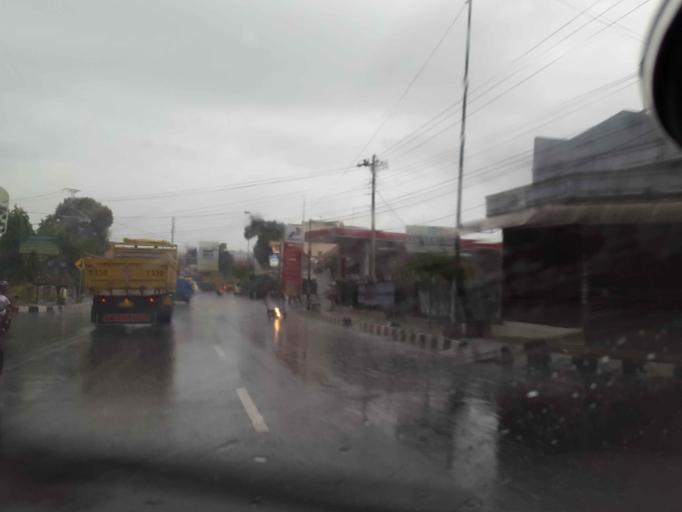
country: ID
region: Central Java
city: Kutoarjo
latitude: -7.7078
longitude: 110.0144
